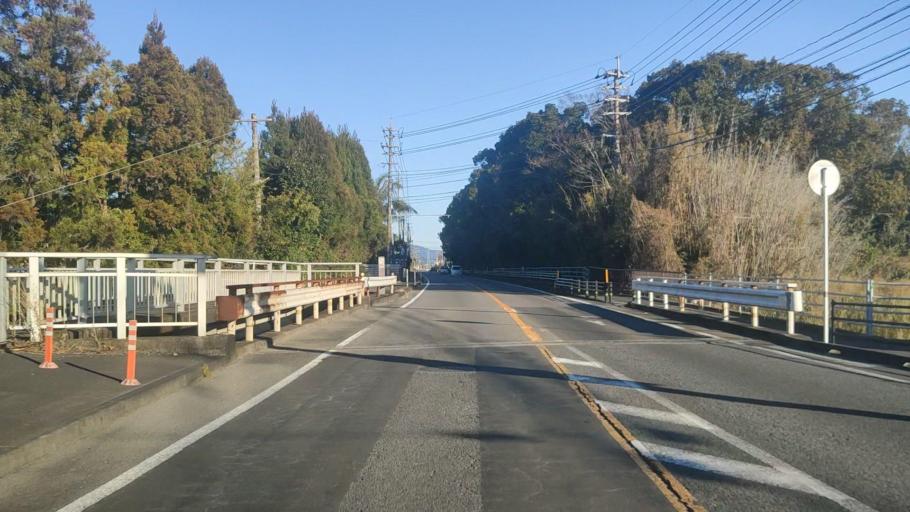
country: JP
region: Miyazaki
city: Nobeoka
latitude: 32.3803
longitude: 131.6277
